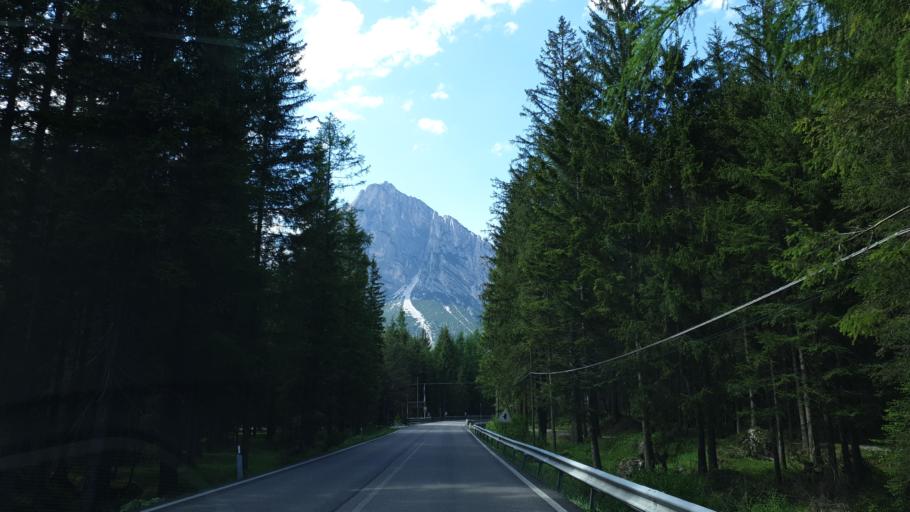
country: IT
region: Veneto
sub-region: Provincia di Belluno
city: Cortina d'Ampezzo
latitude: 46.5681
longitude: 12.1200
